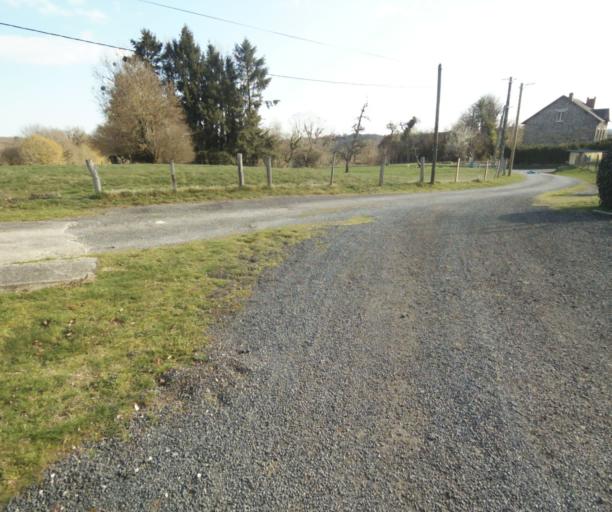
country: FR
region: Limousin
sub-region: Departement de la Correze
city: Saint-Mexant
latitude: 45.3393
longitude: 1.5951
